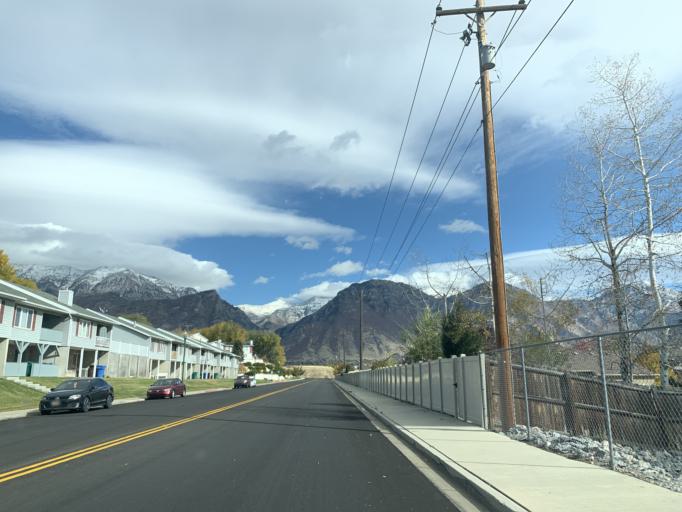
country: US
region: Utah
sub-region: Utah County
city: Provo
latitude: 40.2605
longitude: -111.6844
